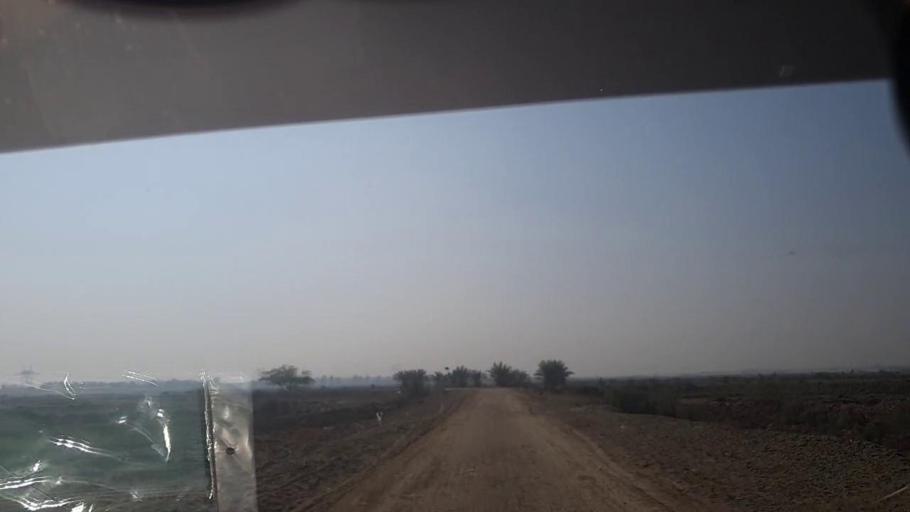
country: PK
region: Sindh
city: Khairpur
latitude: 27.4618
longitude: 68.7380
